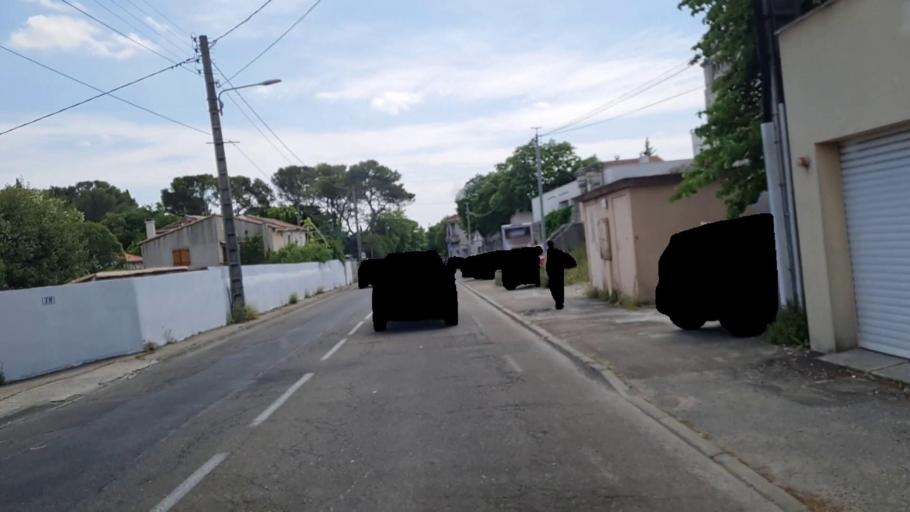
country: FR
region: Languedoc-Roussillon
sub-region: Departement du Gard
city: Nimes
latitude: 43.8368
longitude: 4.3330
